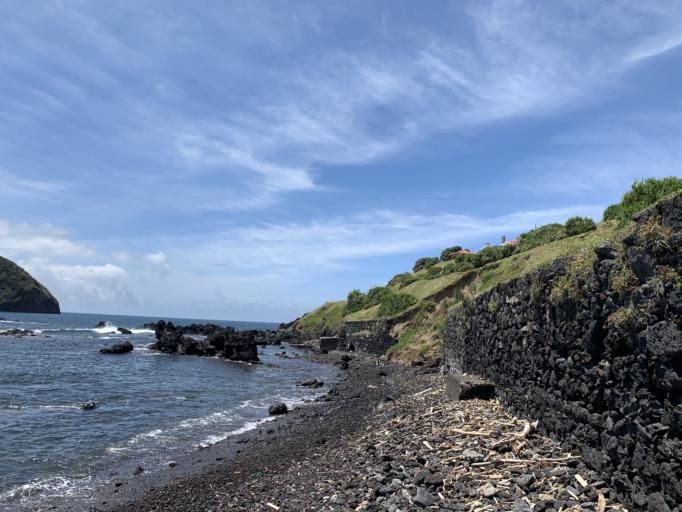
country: PT
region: Azores
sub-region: Vila Franca do Campo
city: Vila Franca do Campo
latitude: 37.7128
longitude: -25.4416
